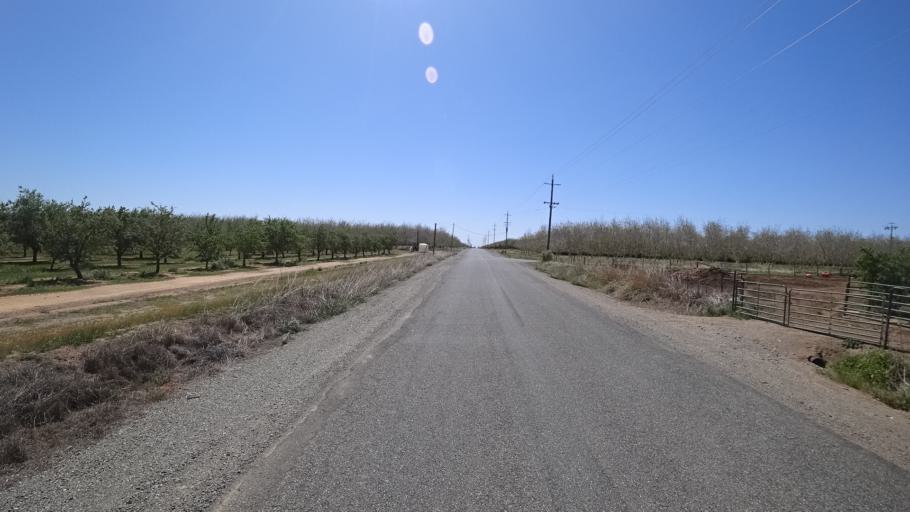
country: US
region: California
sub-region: Glenn County
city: Orland
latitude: 39.7873
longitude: -122.1410
